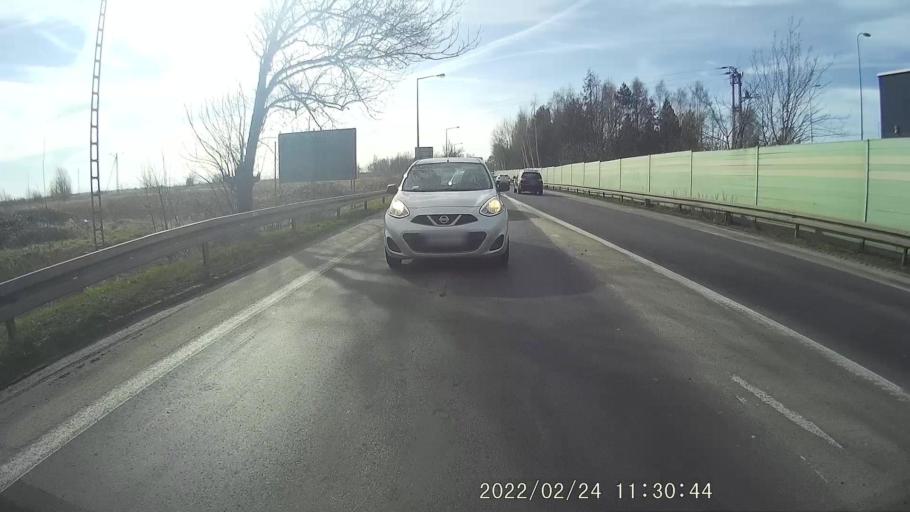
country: PL
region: Lower Silesian Voivodeship
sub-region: Powiat polkowicki
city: Przemkow
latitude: 51.5222
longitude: 15.7230
